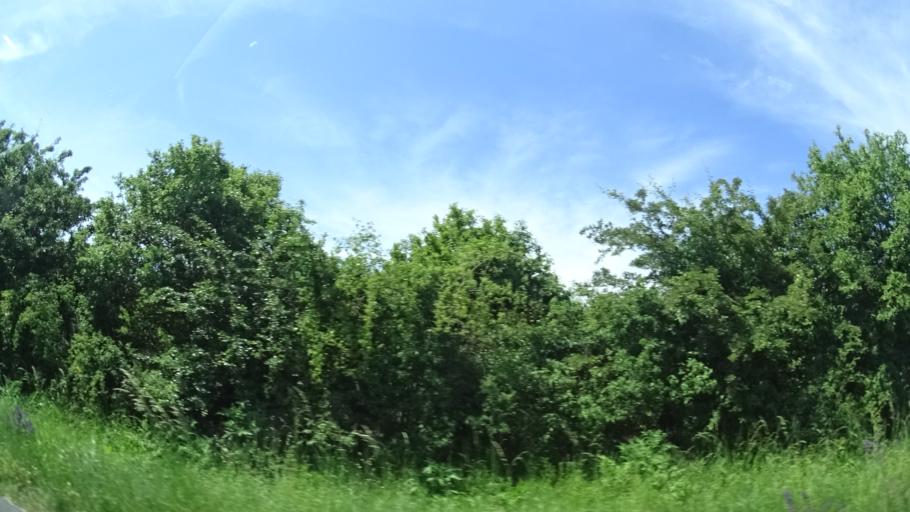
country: DE
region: Bavaria
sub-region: Regierungsbezirk Unterfranken
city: Oerlenbach
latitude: 50.1691
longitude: 10.1499
